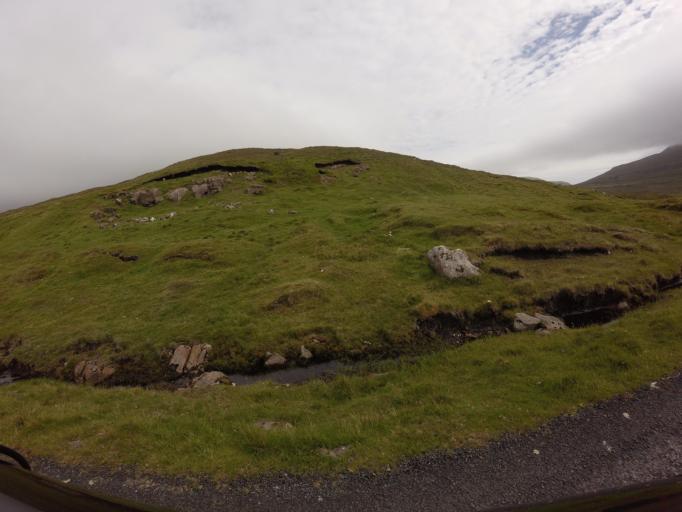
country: FO
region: Sandoy
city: Sandur
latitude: 61.8236
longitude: -6.7579
